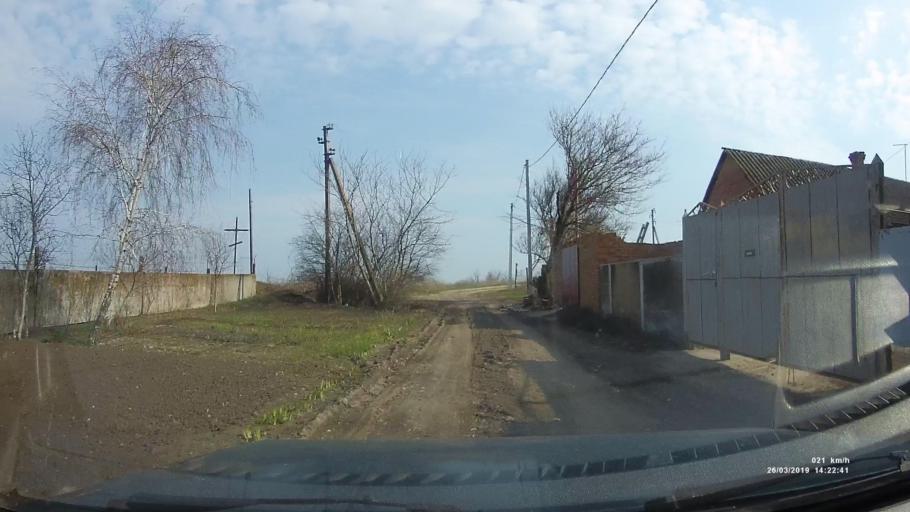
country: RU
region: Rostov
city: Novobessergenovka
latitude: 47.1839
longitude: 38.8702
